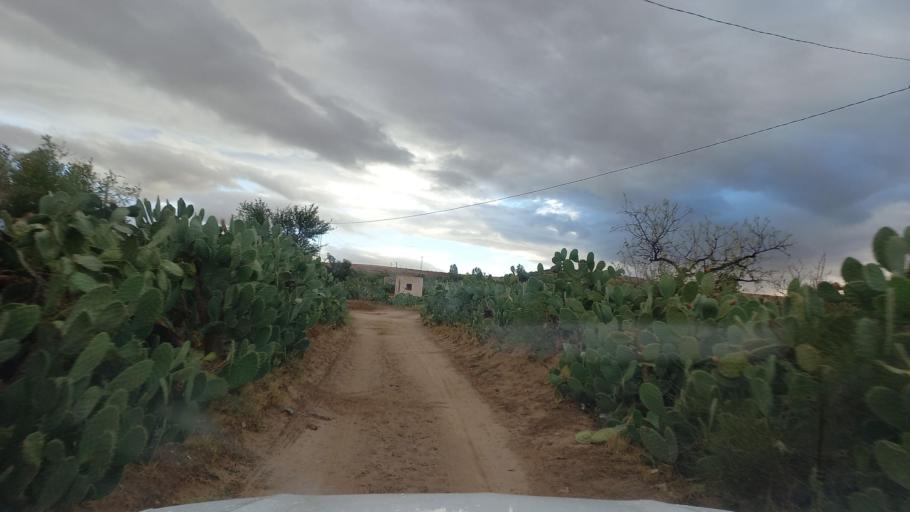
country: TN
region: Al Qasrayn
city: Kasserine
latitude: 35.2609
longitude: 8.9348
